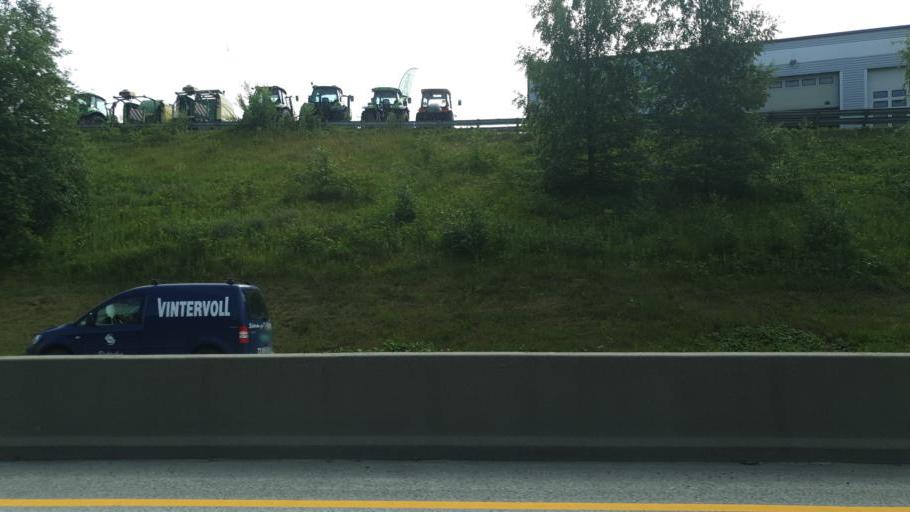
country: NO
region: Sor-Trondelag
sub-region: Melhus
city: Melhus
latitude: 63.2916
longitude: 10.2728
